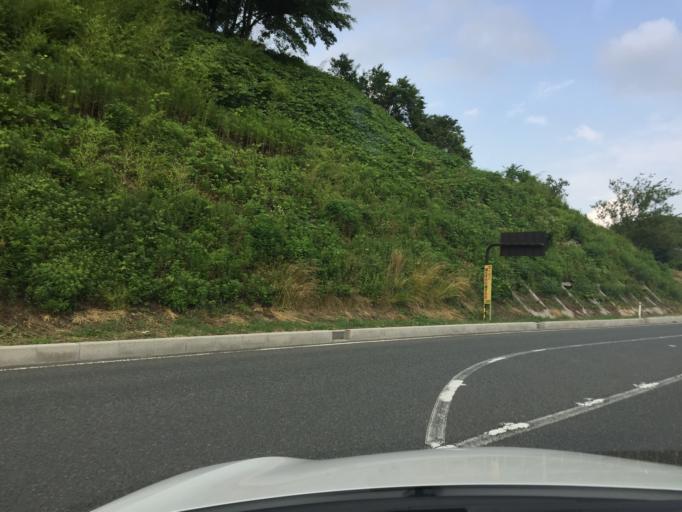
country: JP
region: Fukushima
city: Miharu
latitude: 37.3959
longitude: 140.4857
